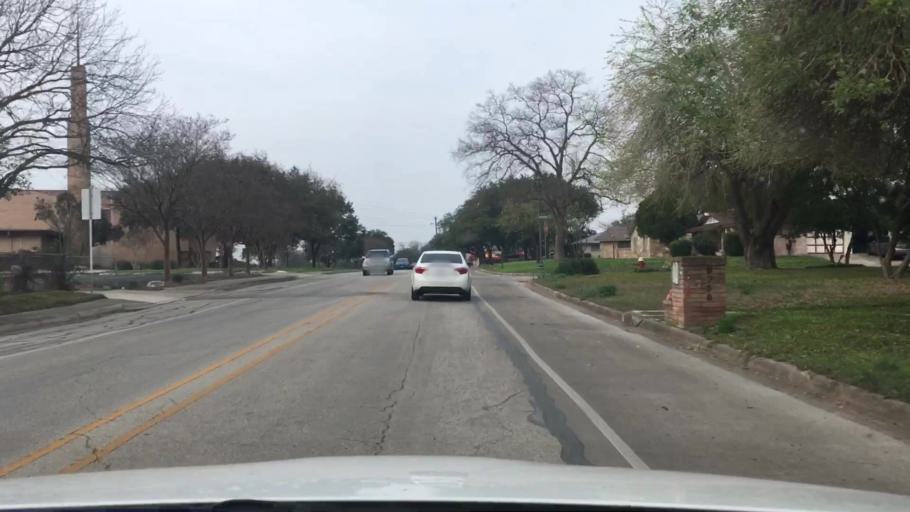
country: US
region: Texas
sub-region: Bexar County
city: Windcrest
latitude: 29.5213
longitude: -98.3816
